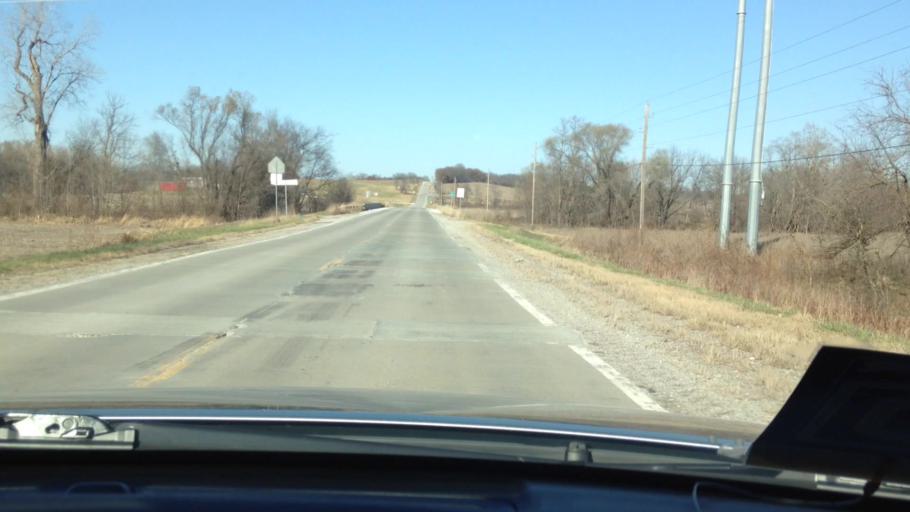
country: US
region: Missouri
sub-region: Platte County
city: Platte City
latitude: 39.5051
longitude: -94.7993
